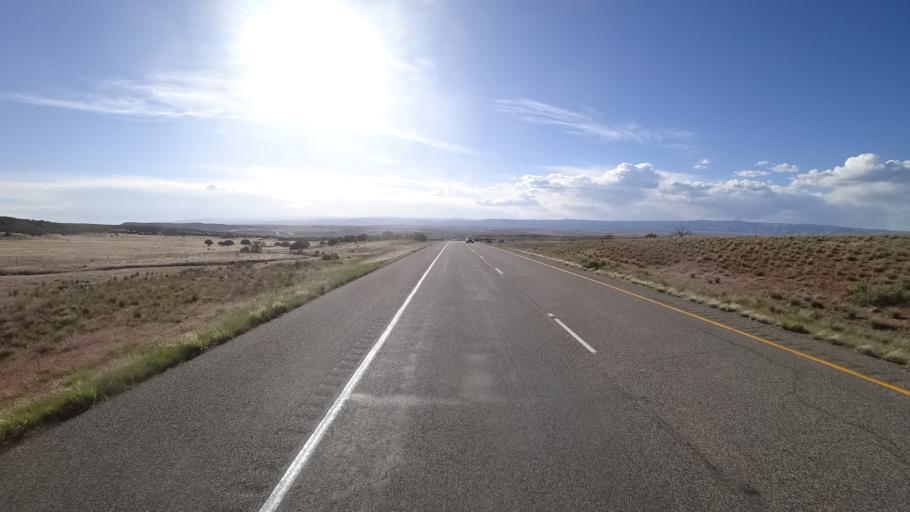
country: US
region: Colorado
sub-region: Mesa County
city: Loma
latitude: 39.1894
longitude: -109.0416
